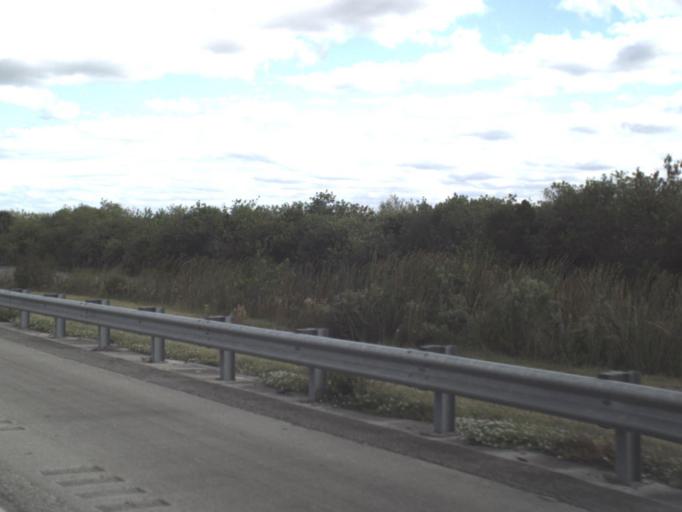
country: US
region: Florida
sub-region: Saint Lucie County
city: Lakewood Park
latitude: 27.4850
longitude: -80.5340
